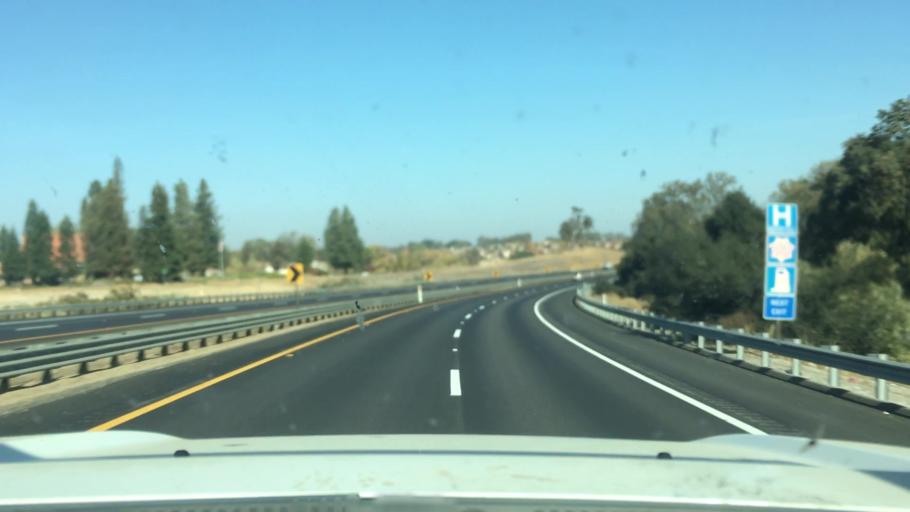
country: US
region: California
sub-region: San Luis Obispo County
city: Templeton
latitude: 35.5582
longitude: -120.7122
